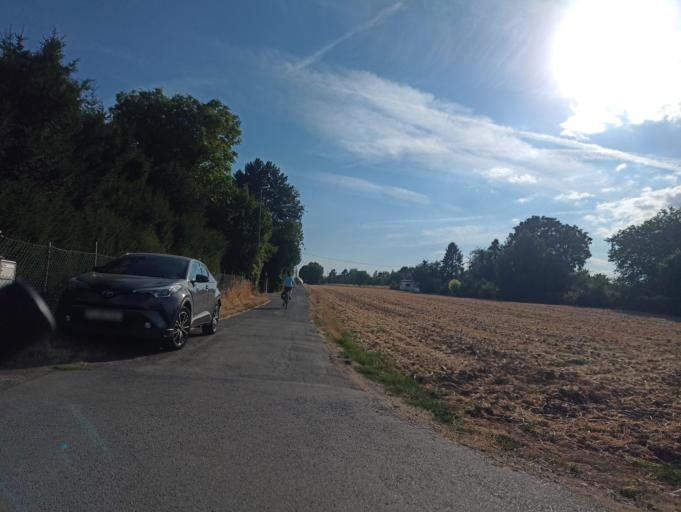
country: DE
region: Hesse
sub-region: Regierungsbezirk Darmstadt
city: Bad Vilbel
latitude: 50.1927
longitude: 8.6762
